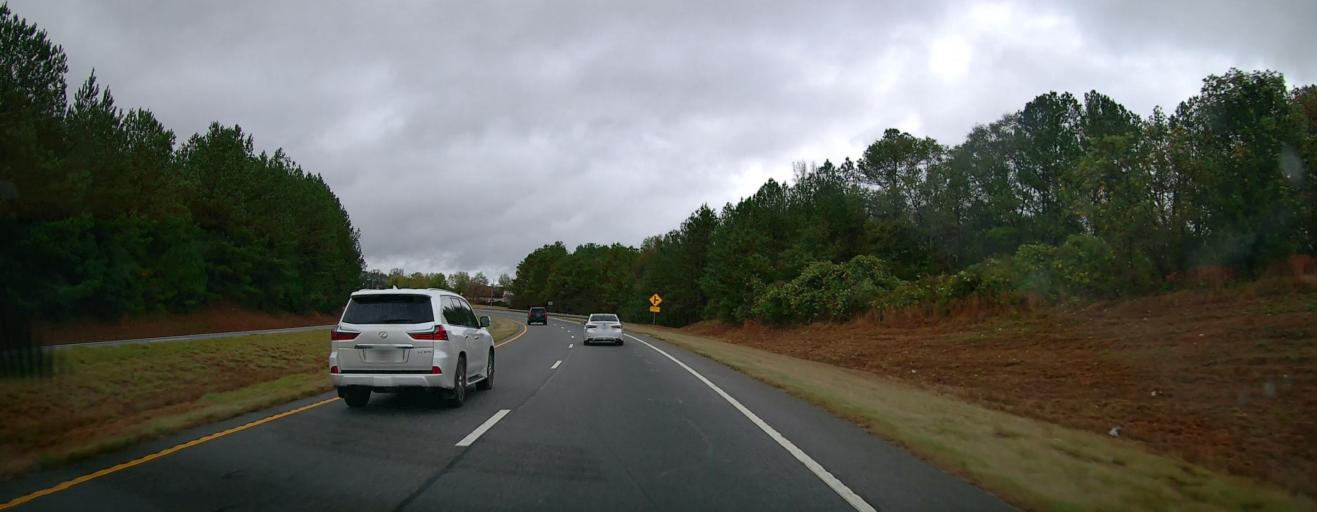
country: US
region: Georgia
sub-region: Oconee County
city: Watkinsville
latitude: 33.8833
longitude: -83.4135
